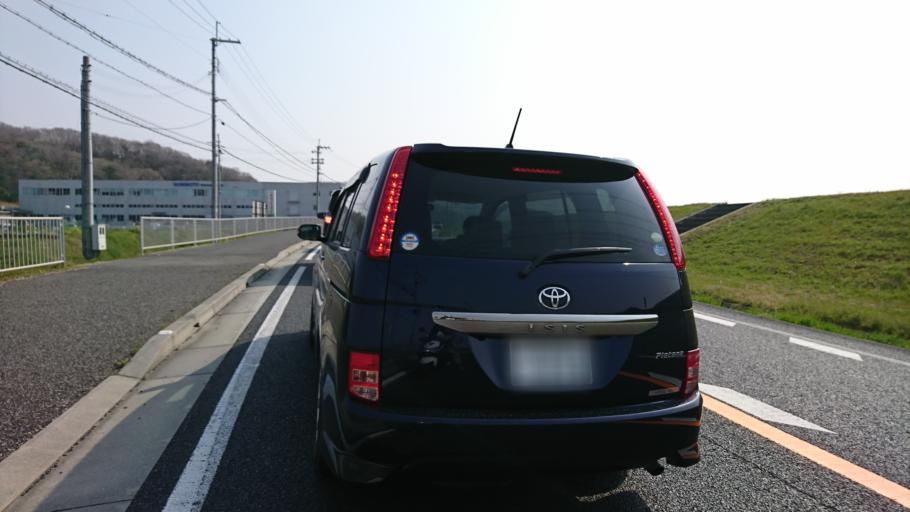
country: JP
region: Hyogo
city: Ono
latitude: 34.8188
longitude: 134.9388
